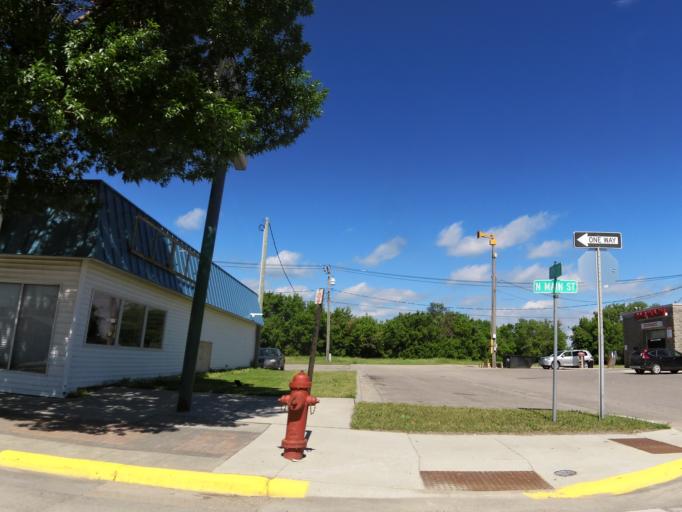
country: US
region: Minnesota
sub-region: Polk County
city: Crookston
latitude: 47.7770
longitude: -96.6062
